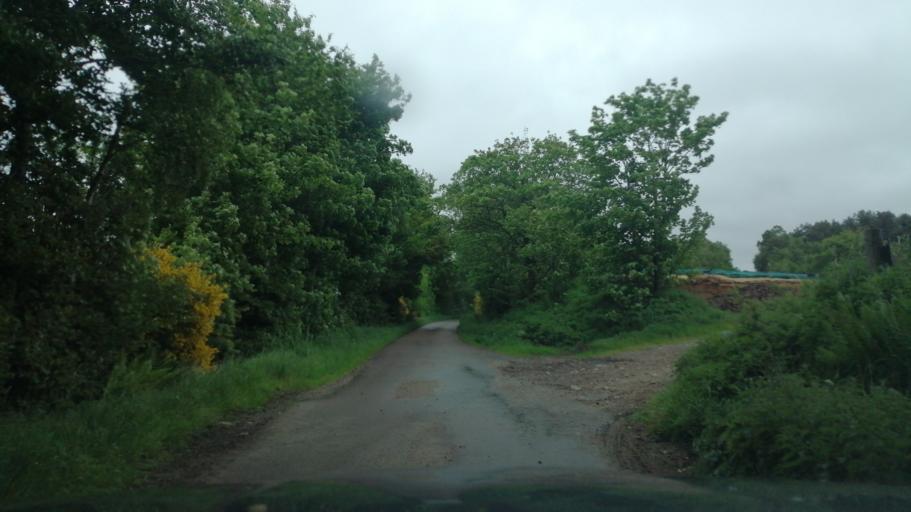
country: GB
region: Scotland
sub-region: Moray
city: Keith
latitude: 57.5629
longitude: -2.8618
